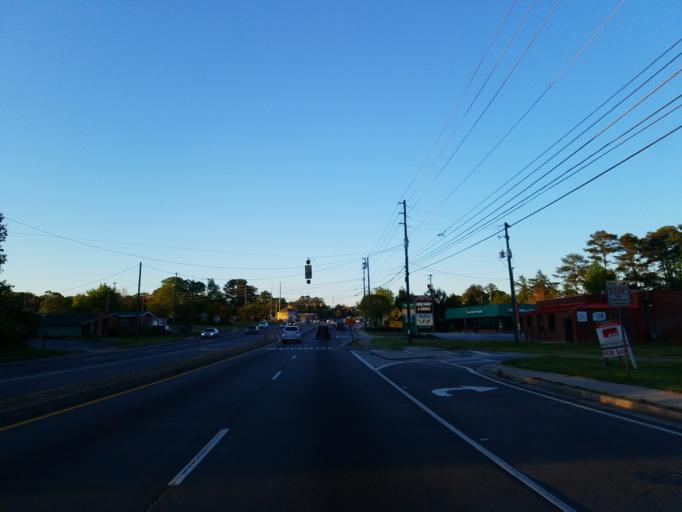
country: US
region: Georgia
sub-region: Cobb County
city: Fair Oaks
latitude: 33.8934
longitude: -84.5772
